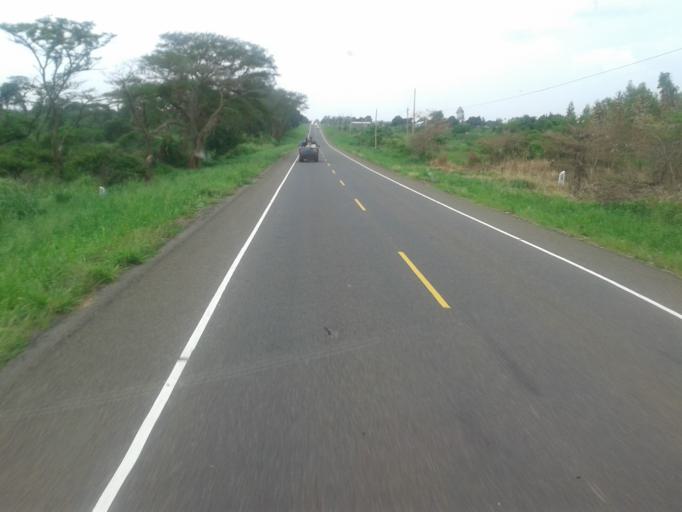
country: UG
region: Northern Region
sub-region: Oyam District
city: Oyam
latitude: 2.1394
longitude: 32.2066
